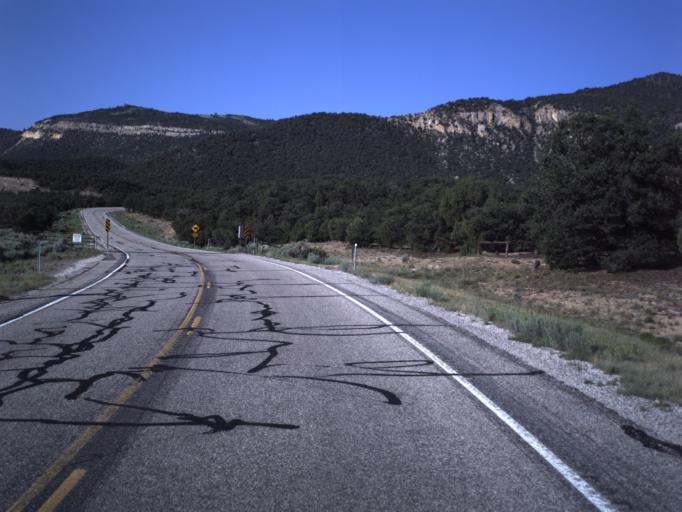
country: US
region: Utah
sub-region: Wayne County
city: Loa
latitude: 38.7315
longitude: -111.3972
